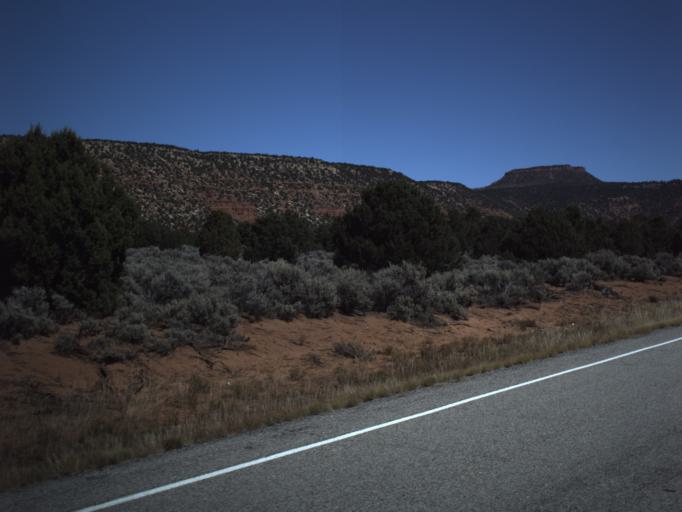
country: US
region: Utah
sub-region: San Juan County
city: Blanding
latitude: 37.5837
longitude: -109.9081
